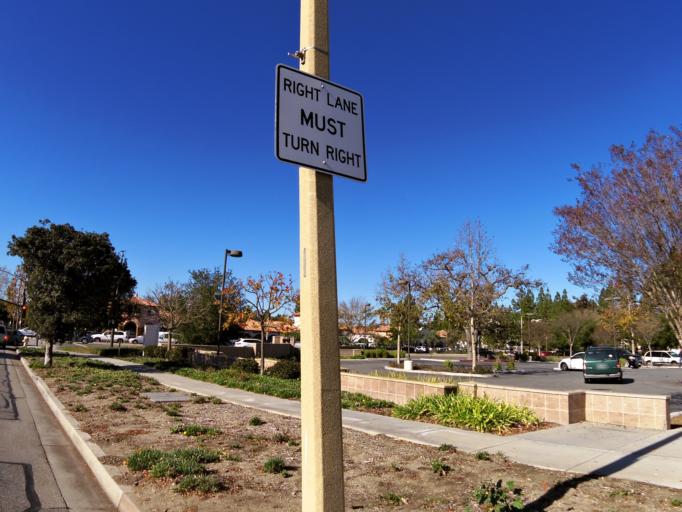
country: US
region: California
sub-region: Ventura County
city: Thousand Oaks
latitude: 34.1792
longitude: -118.8757
